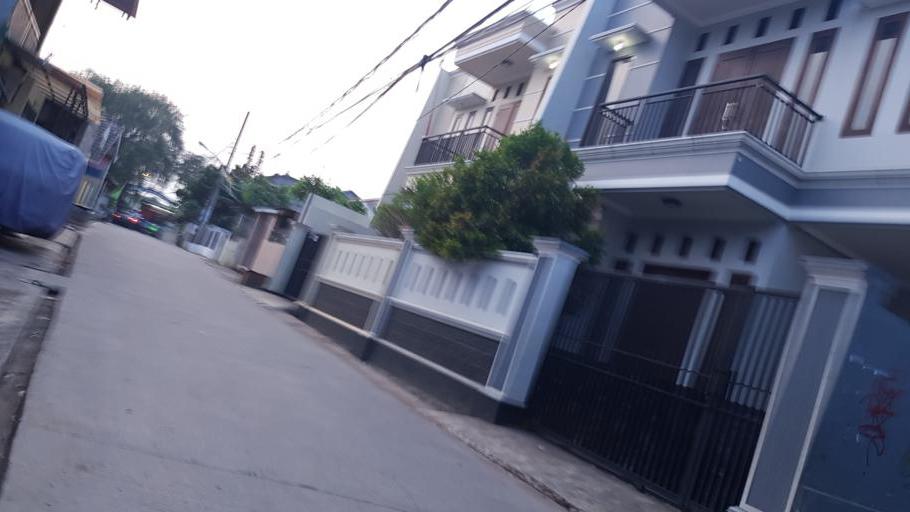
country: ID
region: West Java
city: Bekasi
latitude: -6.2666
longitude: 106.9264
